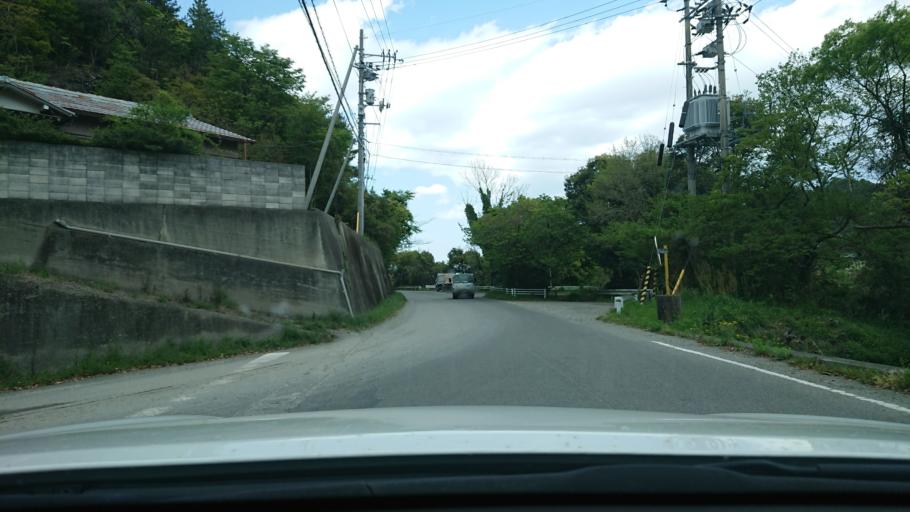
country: JP
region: Tokushima
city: Komatsushimacho
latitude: 33.9834
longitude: 134.5437
